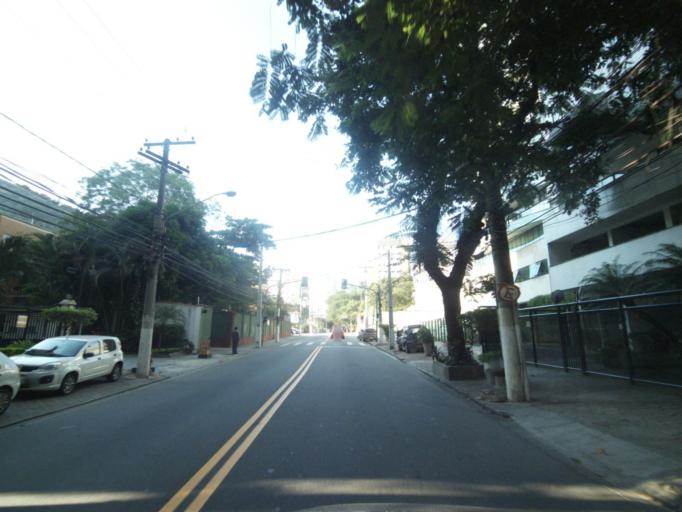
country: BR
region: Rio de Janeiro
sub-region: Niteroi
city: Niteroi
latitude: -22.8953
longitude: -43.0999
